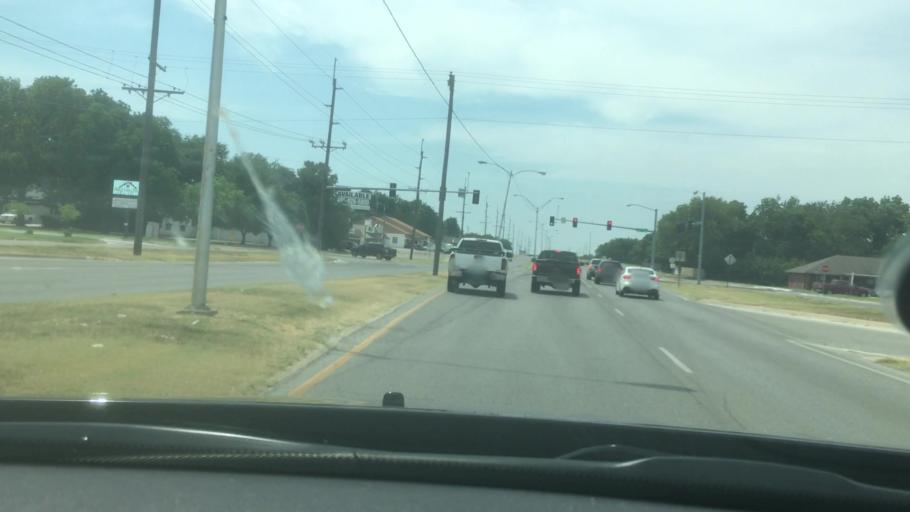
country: US
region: Oklahoma
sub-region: Carter County
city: Ardmore
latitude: 34.1719
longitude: -97.1434
